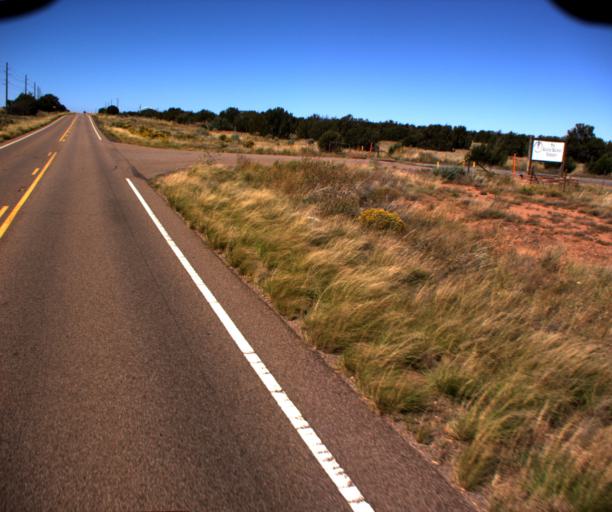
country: US
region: Arizona
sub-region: Navajo County
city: Taylor
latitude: 34.4829
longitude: -110.3135
